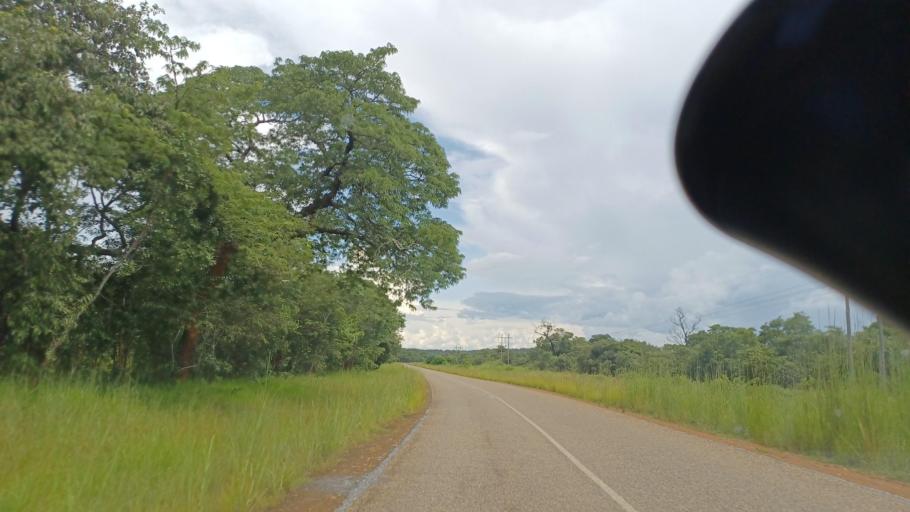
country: ZM
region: North-Western
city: Kasempa
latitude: -13.1548
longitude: 25.8782
